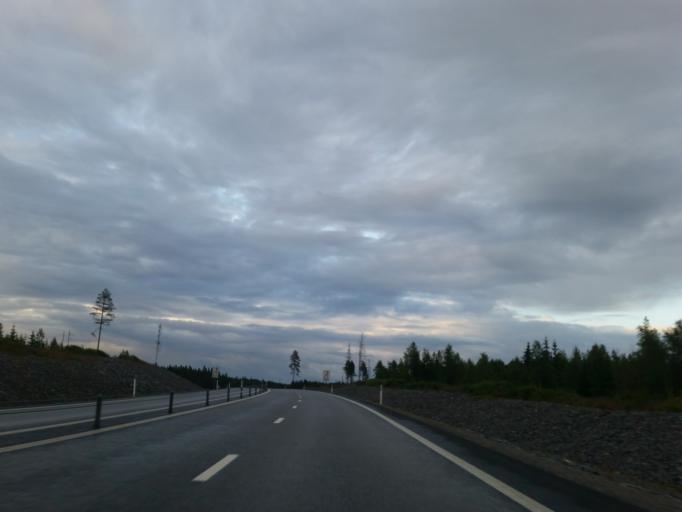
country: SE
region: Vaesterbotten
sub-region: Umea Kommun
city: Umea
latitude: 63.8546
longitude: 20.2666
